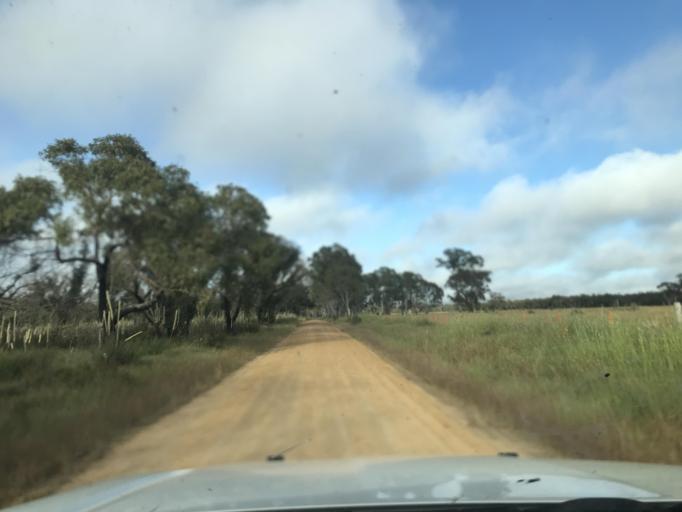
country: AU
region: South Australia
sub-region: Wattle Range
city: Penola
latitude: -37.1805
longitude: 141.1837
